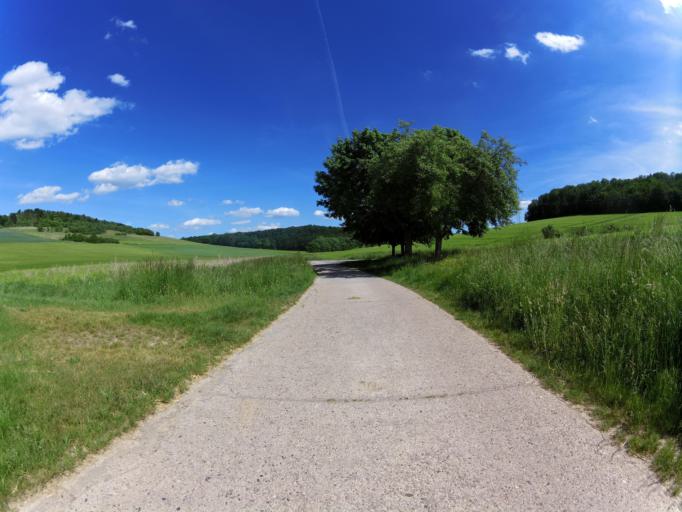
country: DE
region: Bavaria
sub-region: Regierungsbezirk Unterfranken
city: Uettingen
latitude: 49.7909
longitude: 9.7384
